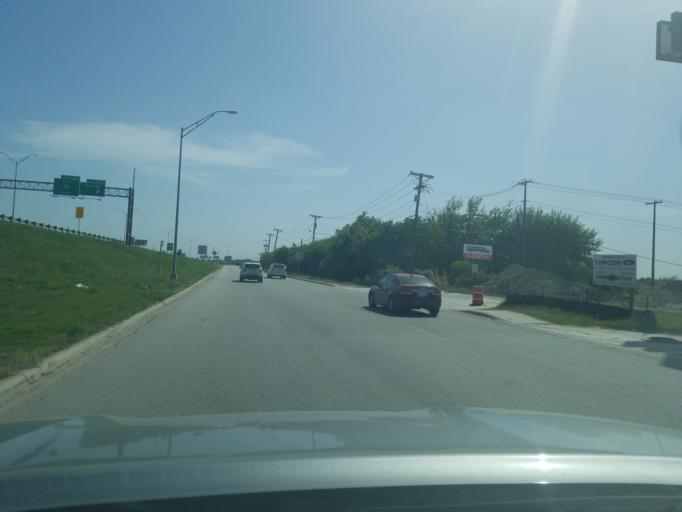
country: US
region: Texas
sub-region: Comal County
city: New Braunfels
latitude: 29.7288
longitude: -98.0791
